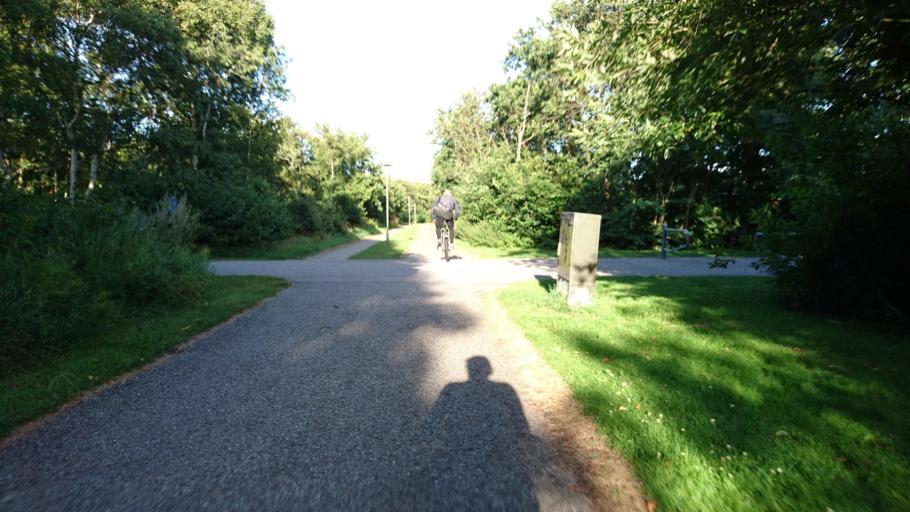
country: DK
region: North Denmark
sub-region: Frederikshavn Kommune
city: Skagen
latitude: 57.7314
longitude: 10.5981
